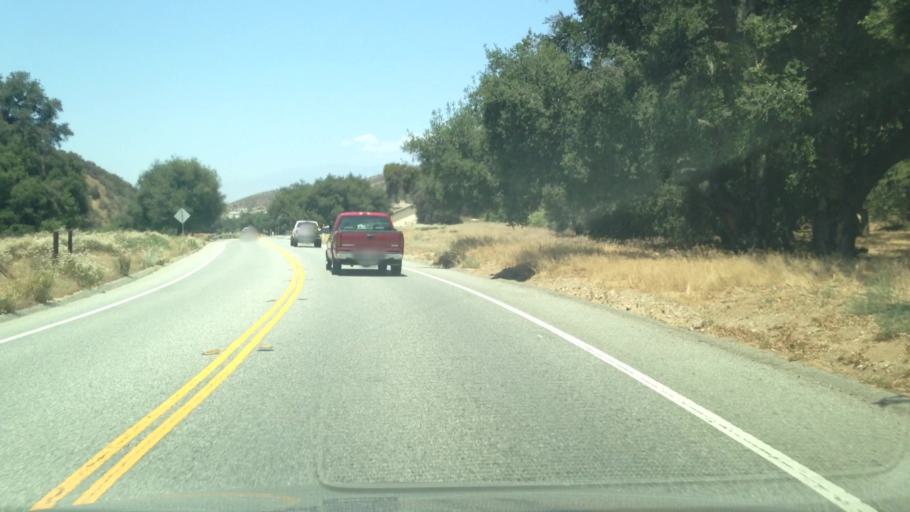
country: US
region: California
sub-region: Riverside County
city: Cherry Valley
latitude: 34.0135
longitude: -116.9956
